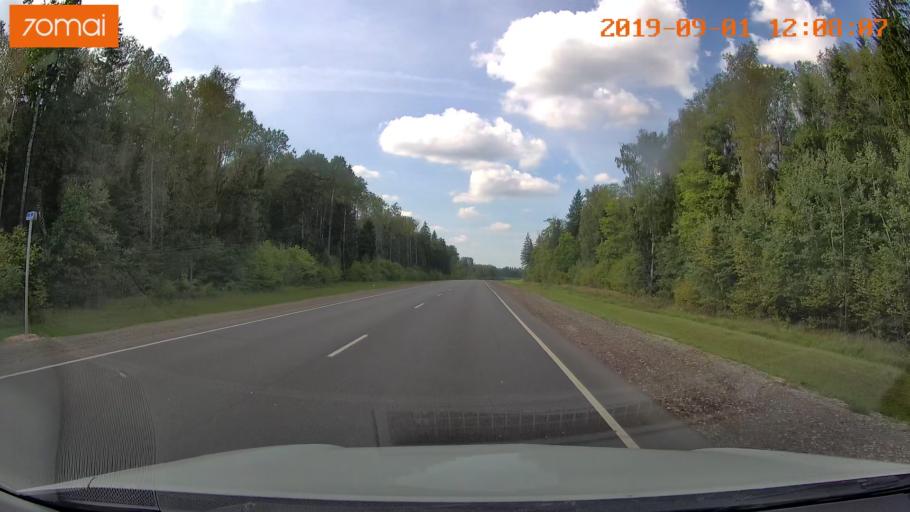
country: RU
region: Kaluga
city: Maloyaroslavets
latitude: 54.9786
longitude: 36.4547
